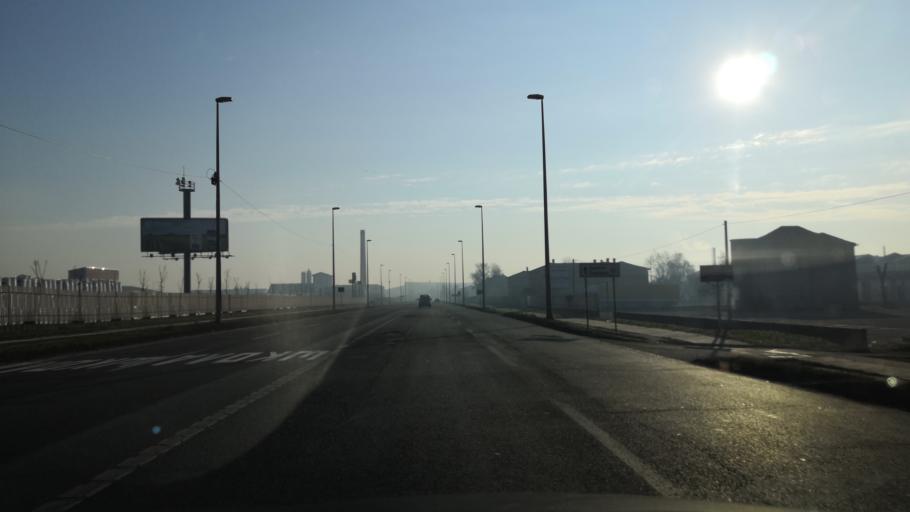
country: RS
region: Central Serbia
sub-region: Macvanski Okrug
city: Sabac
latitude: 44.7489
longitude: 19.7125
